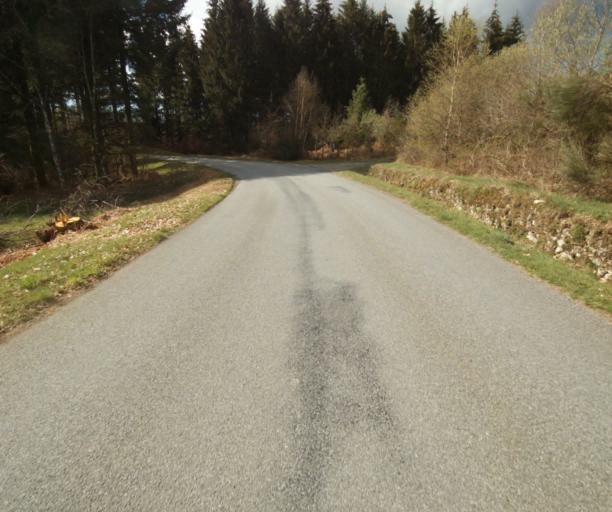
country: FR
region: Limousin
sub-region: Departement de la Correze
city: Argentat
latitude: 45.2347
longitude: 1.9352
